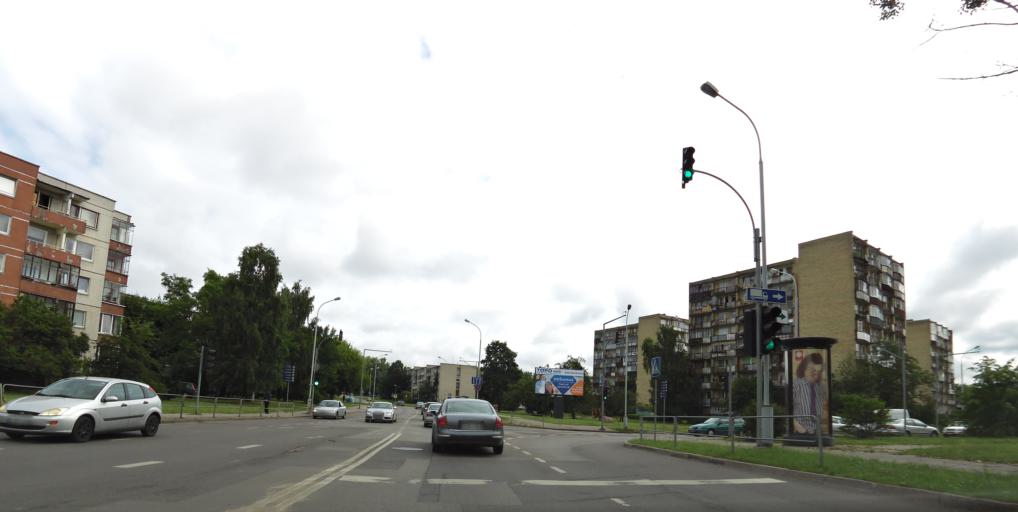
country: LT
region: Vilnius County
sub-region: Vilnius
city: Vilnius
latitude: 54.7038
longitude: 25.2886
